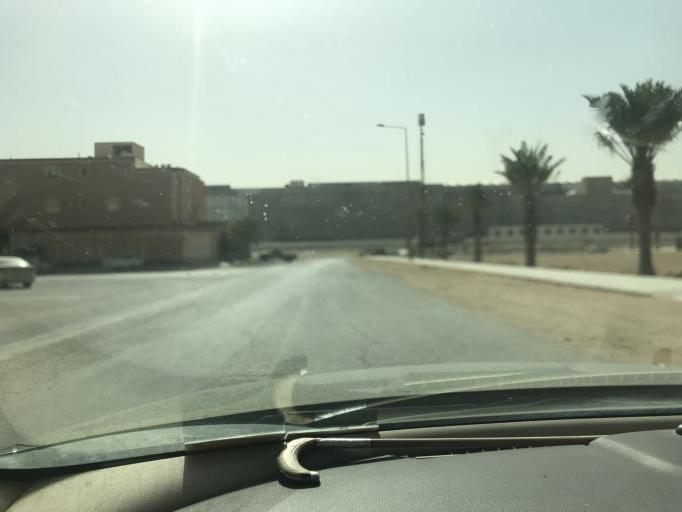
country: SA
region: Ar Riyad
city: Riyadh
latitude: 24.8278
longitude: 46.7309
